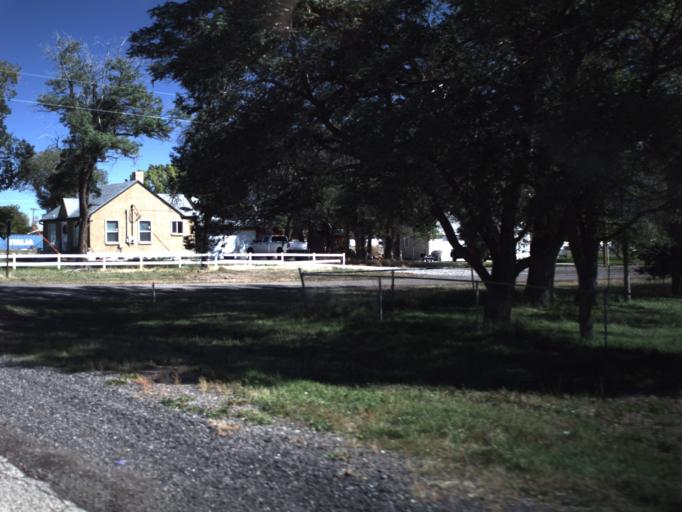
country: US
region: Utah
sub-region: Wayne County
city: Loa
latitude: 38.5081
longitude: -111.8813
